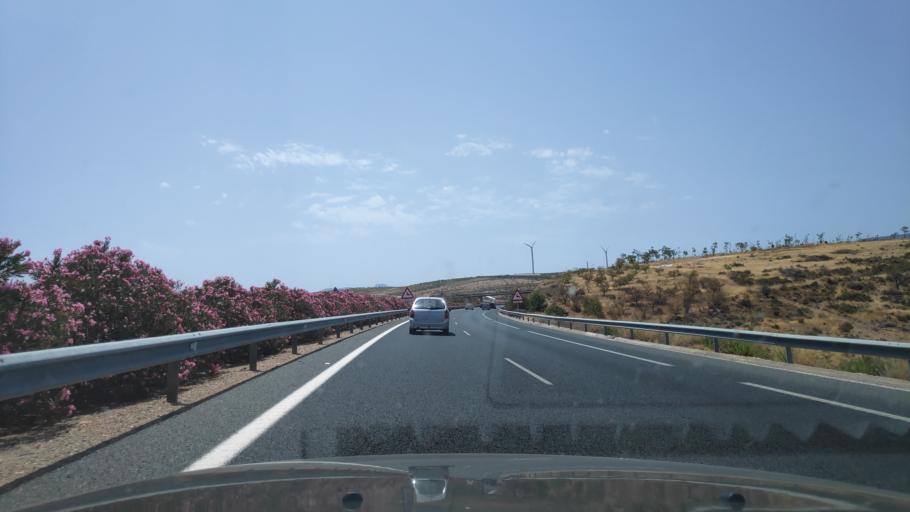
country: ES
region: Andalusia
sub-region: Provincia de Granada
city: Padul
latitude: 37.0165
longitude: -3.6402
